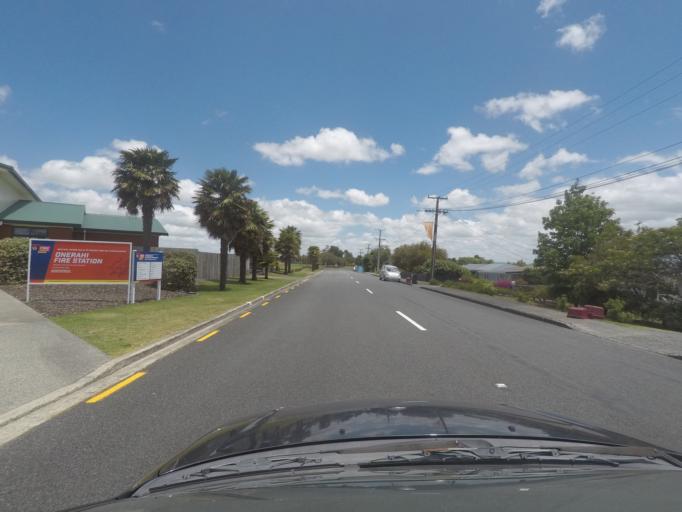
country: NZ
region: Northland
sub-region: Whangarei
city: Whangarei
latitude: -35.7651
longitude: 174.3668
